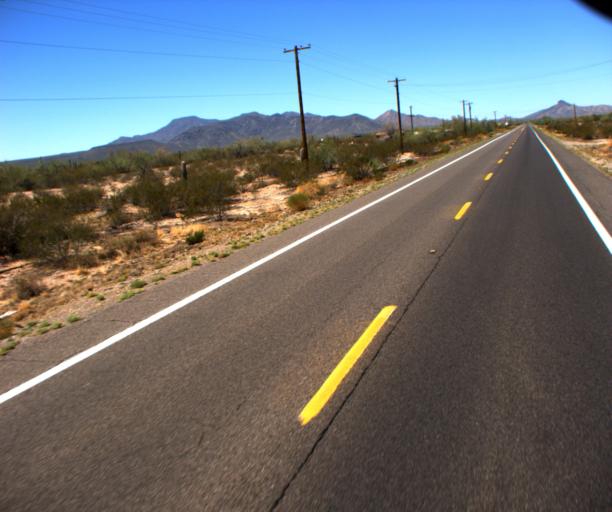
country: US
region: Arizona
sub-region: Pinal County
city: Maricopa
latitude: 32.8572
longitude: -112.0799
